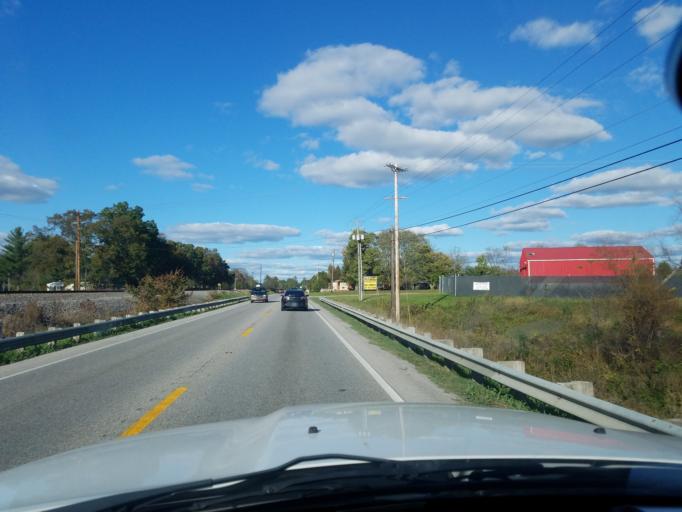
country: US
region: Kentucky
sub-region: Laurel County
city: North Corbin
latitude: 37.0412
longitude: -84.0560
